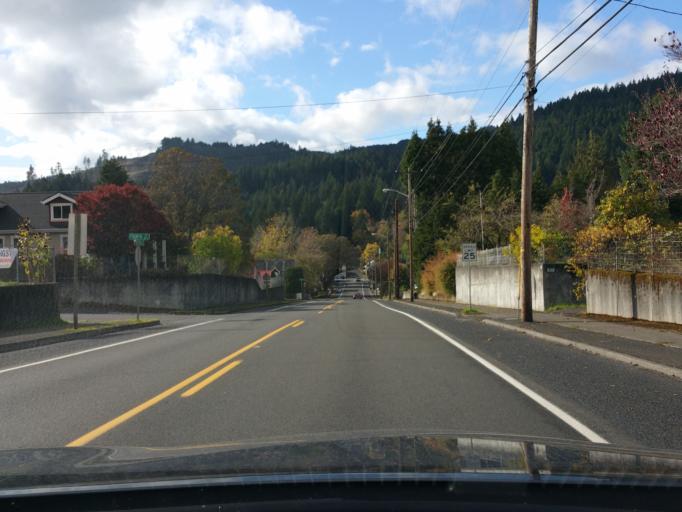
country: US
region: Washington
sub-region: Skamania County
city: Carson
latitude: 45.7259
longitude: -121.8158
